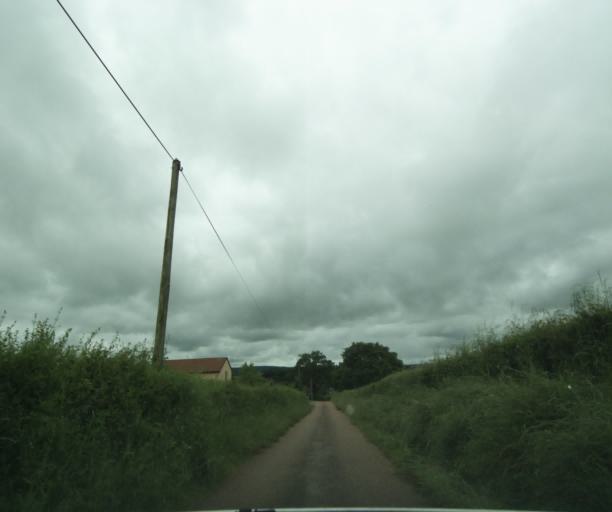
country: FR
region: Bourgogne
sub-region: Departement de Saone-et-Loire
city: Charolles
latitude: 46.4739
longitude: 4.3506
